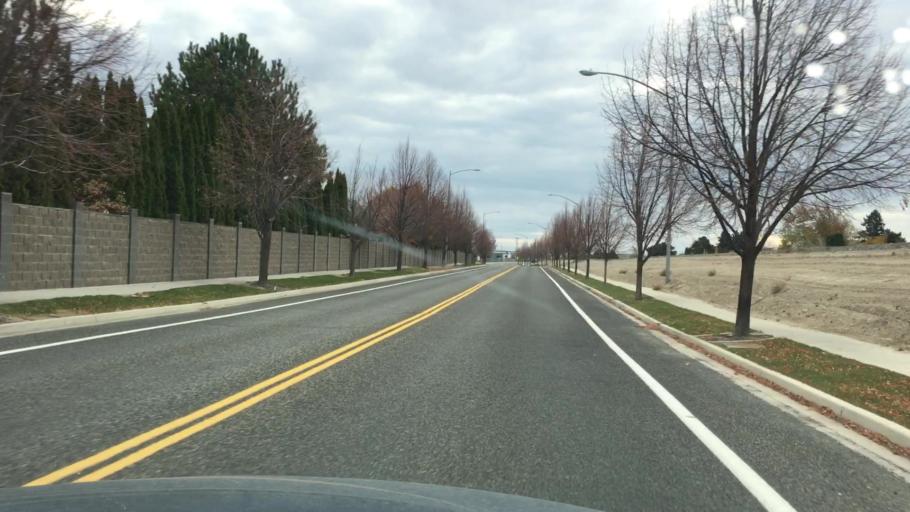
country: US
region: Washington
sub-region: Benton County
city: Kennewick
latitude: 46.1865
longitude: -119.1880
